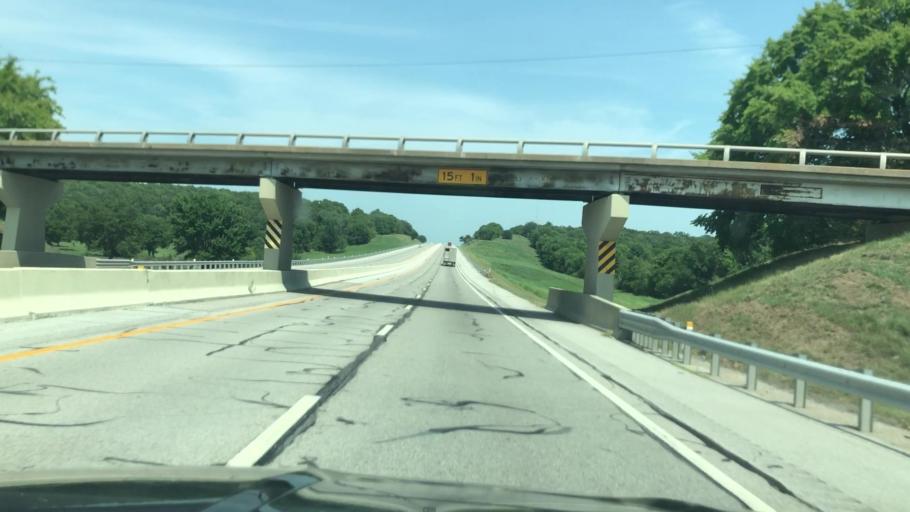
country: US
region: Oklahoma
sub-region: Rogers County
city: Chelsea
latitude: 36.4626
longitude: -95.3461
